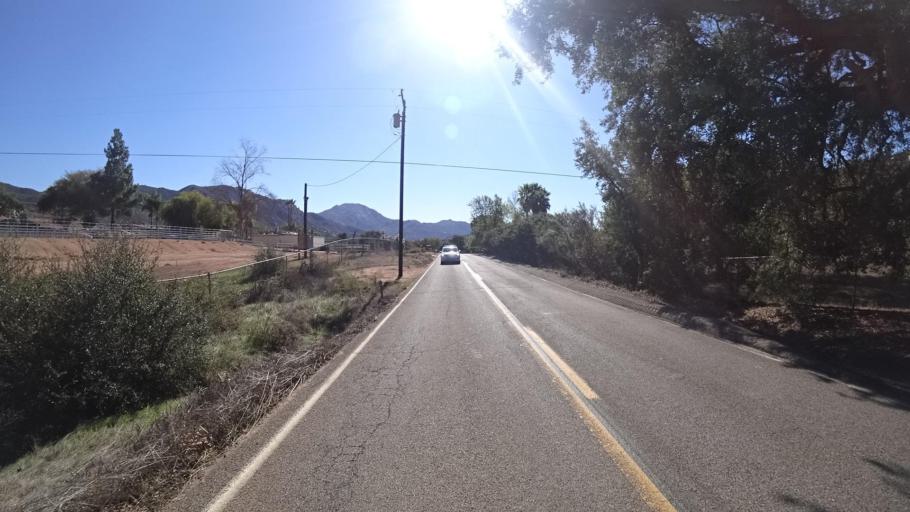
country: US
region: California
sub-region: San Diego County
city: Jamul
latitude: 32.7276
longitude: -116.8175
